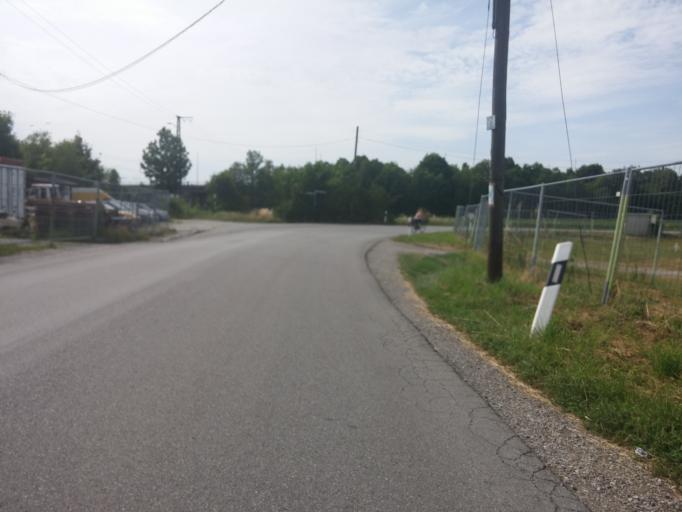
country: DE
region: Bavaria
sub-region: Upper Bavaria
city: Bogenhausen
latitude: 48.1278
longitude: 11.6589
